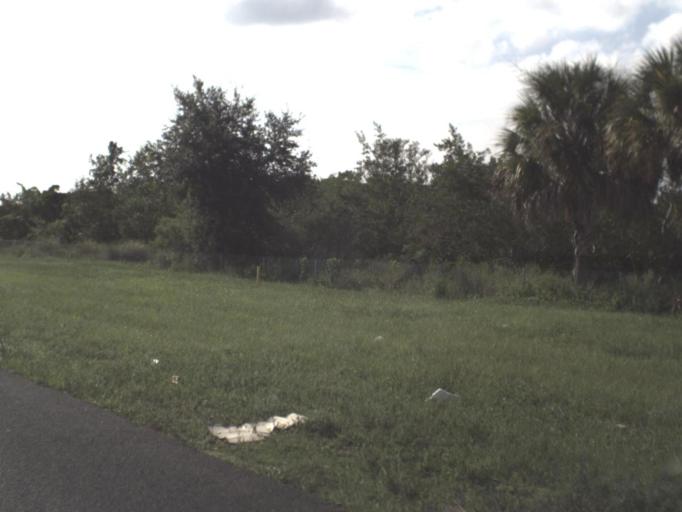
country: US
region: Florida
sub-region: Manatee County
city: Ellenton
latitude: 27.4979
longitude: -82.5208
